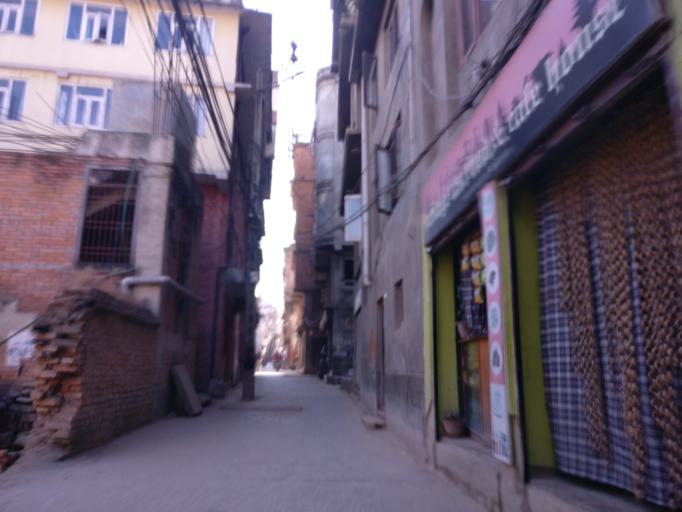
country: NP
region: Central Region
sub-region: Bagmati Zone
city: Patan
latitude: 27.6736
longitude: 85.3278
